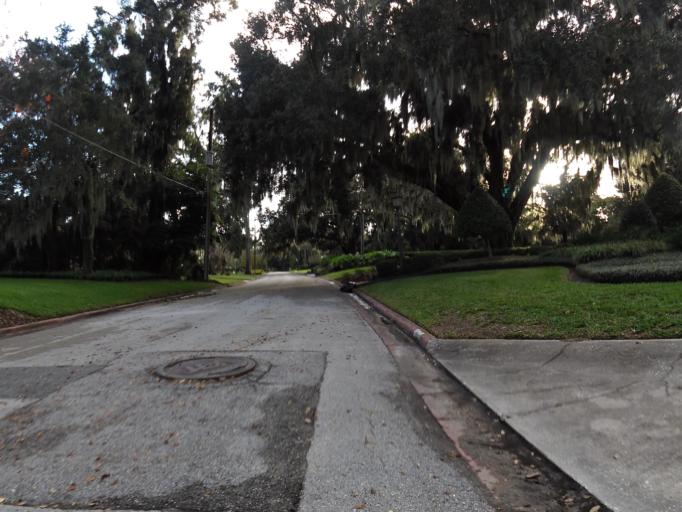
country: US
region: Florida
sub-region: Duval County
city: Jacksonville
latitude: 30.2850
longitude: -81.6611
